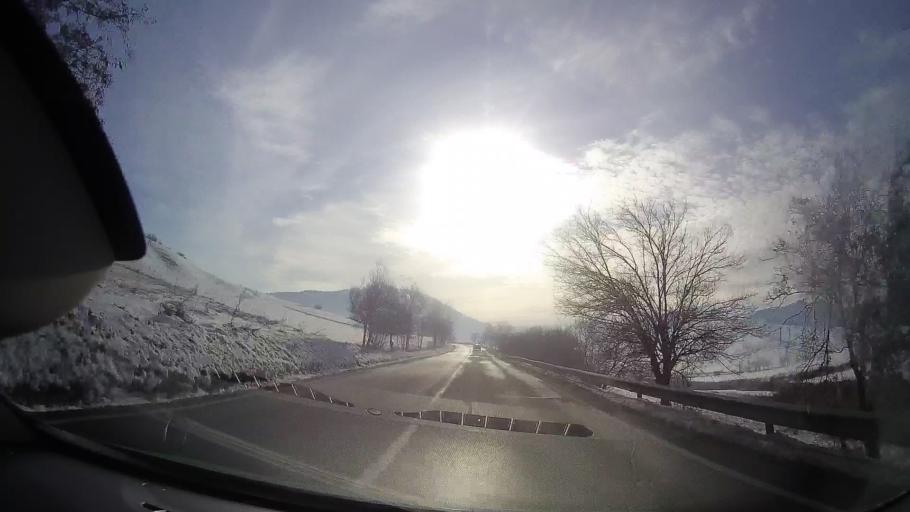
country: RO
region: Neamt
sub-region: Comuna Garcina
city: Garcina
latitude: 46.9849
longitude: 26.3592
